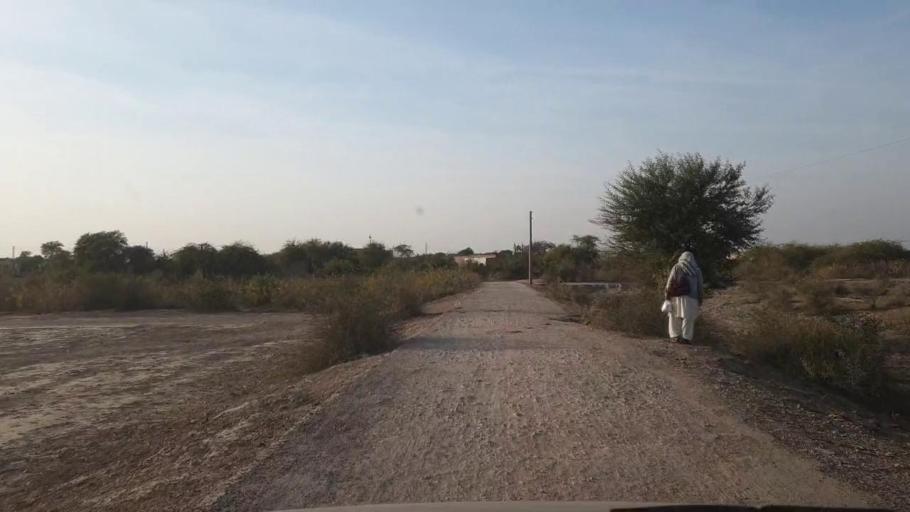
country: PK
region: Sindh
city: Chambar
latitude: 25.2440
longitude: 68.7862
